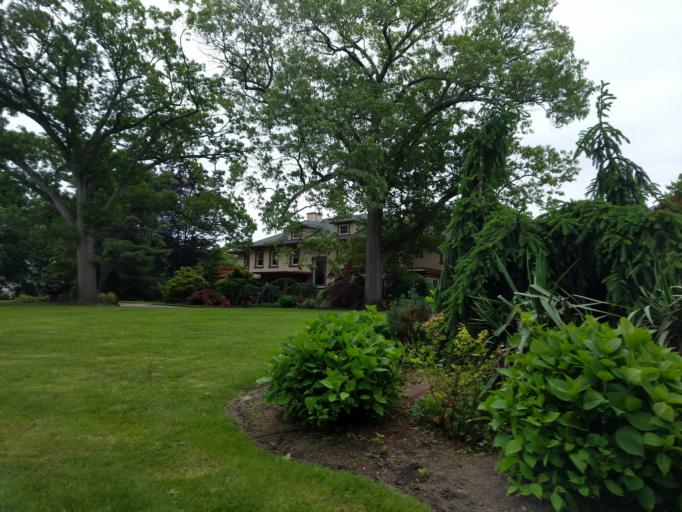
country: US
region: New York
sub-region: Nassau County
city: Hewlett
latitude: 40.6371
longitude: -73.6979
